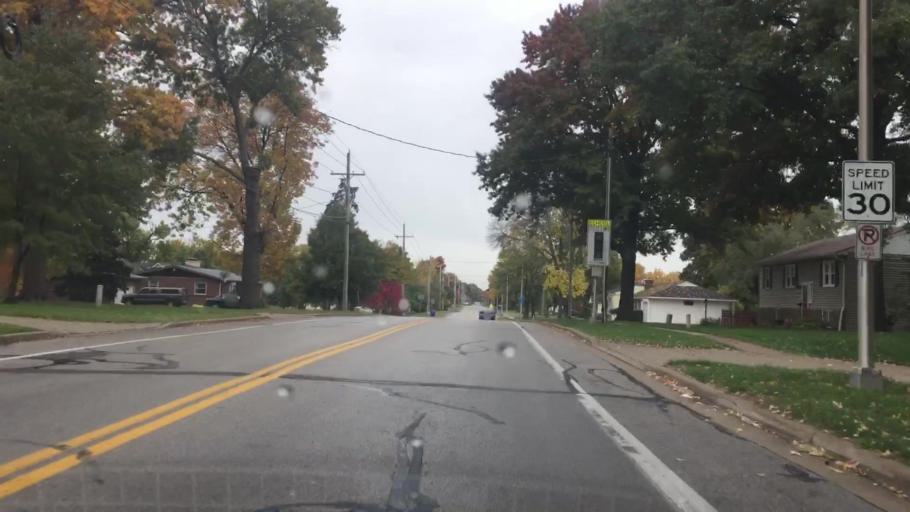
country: US
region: Kansas
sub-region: Johnson County
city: Shawnee
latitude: 39.0289
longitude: -94.7333
